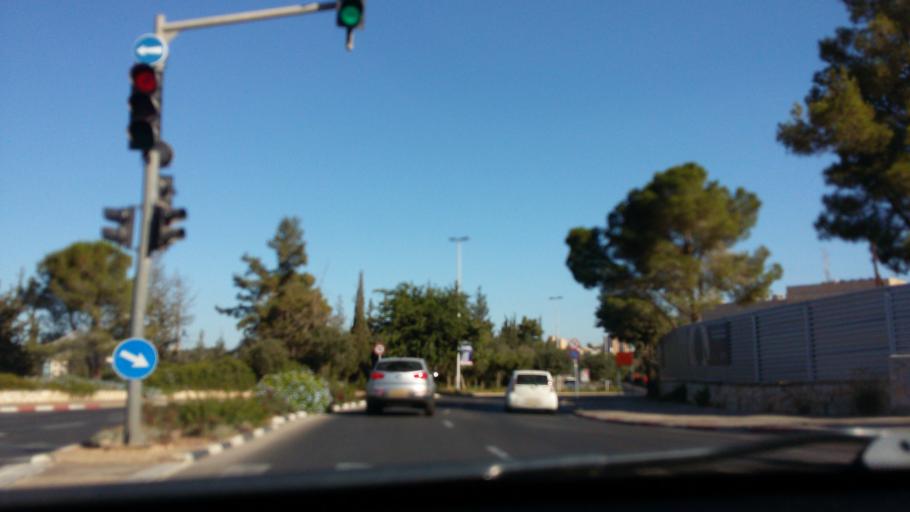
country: IL
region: Jerusalem
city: Jerusalem
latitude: 31.7751
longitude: 35.2042
